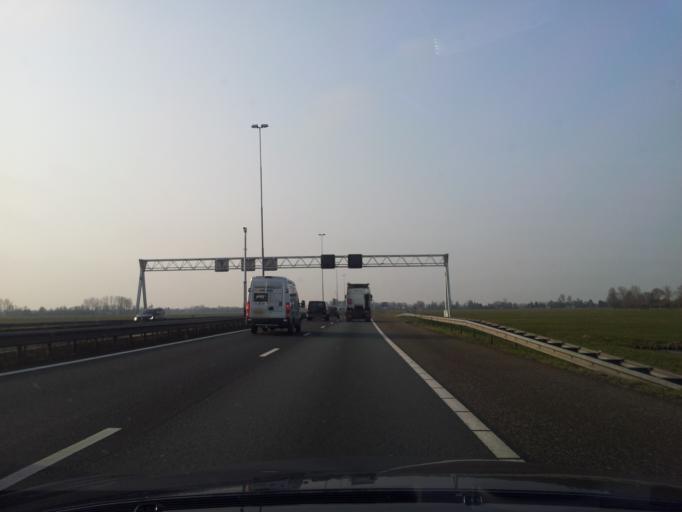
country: NL
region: South Holland
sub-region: Gemeente Gorinchem
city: Gorinchem
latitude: 51.8899
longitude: 4.9752
